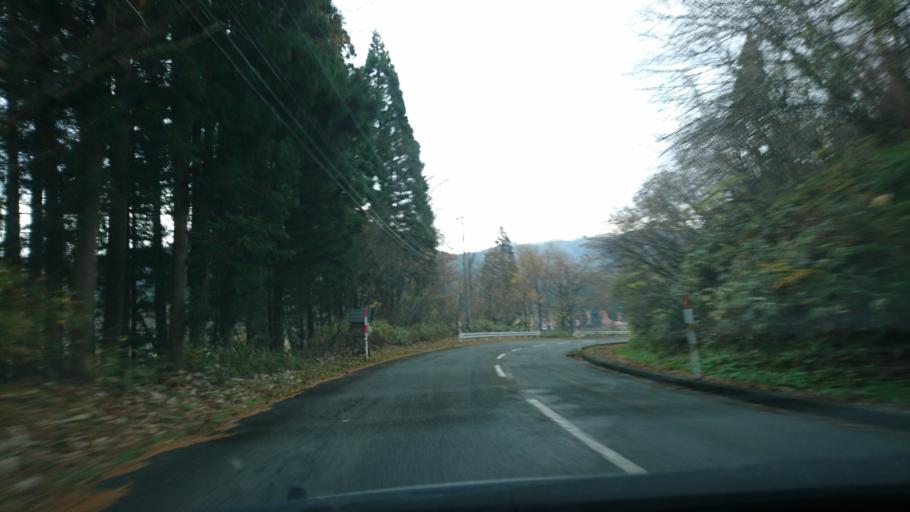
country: JP
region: Iwate
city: Ichinoseki
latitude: 38.9627
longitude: 140.9419
